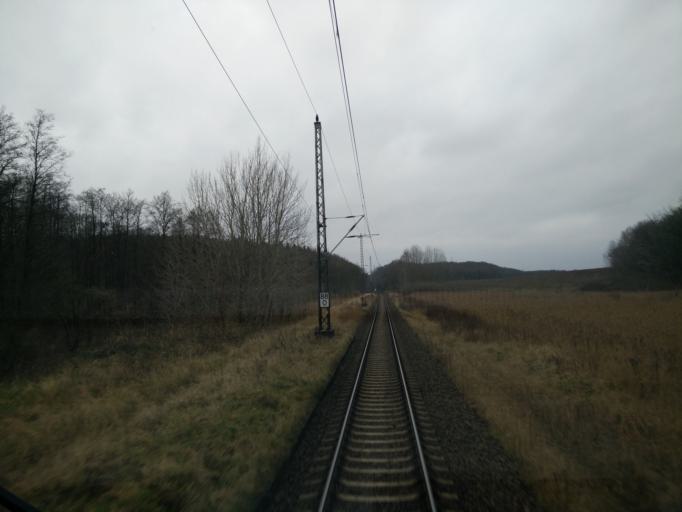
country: DE
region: Mecklenburg-Vorpommern
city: Bad Kleinen
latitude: 53.8078
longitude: 11.4814
